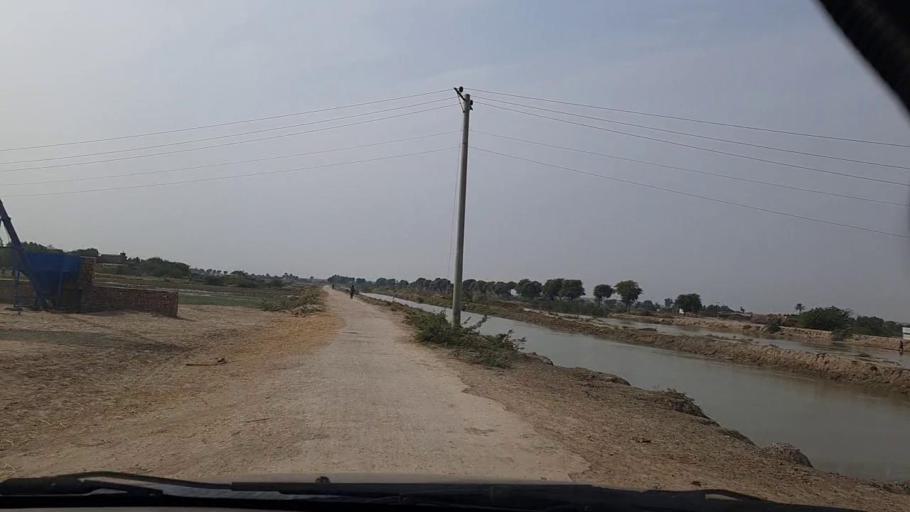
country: PK
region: Sindh
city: Thatta
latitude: 24.5784
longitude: 67.8915
